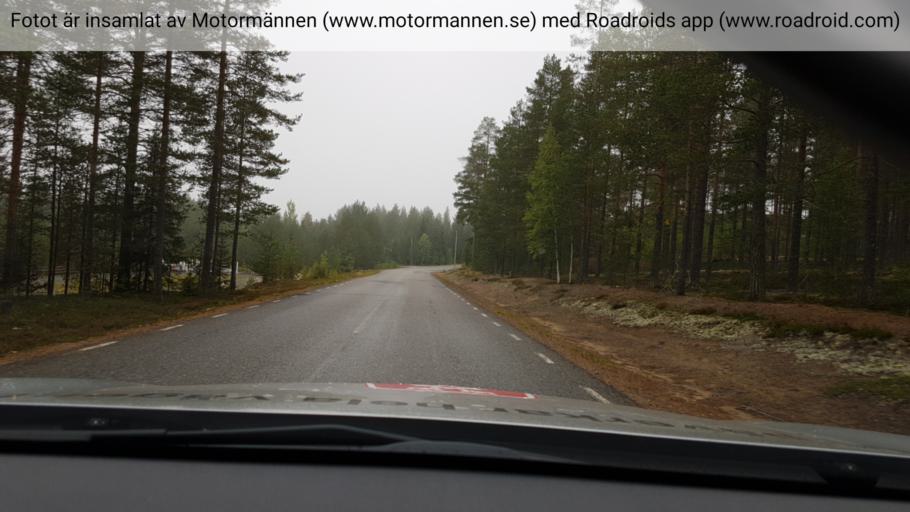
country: SE
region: Vaesterbotten
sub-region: Umea Kommun
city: Ersmark
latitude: 64.2364
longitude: 20.2717
